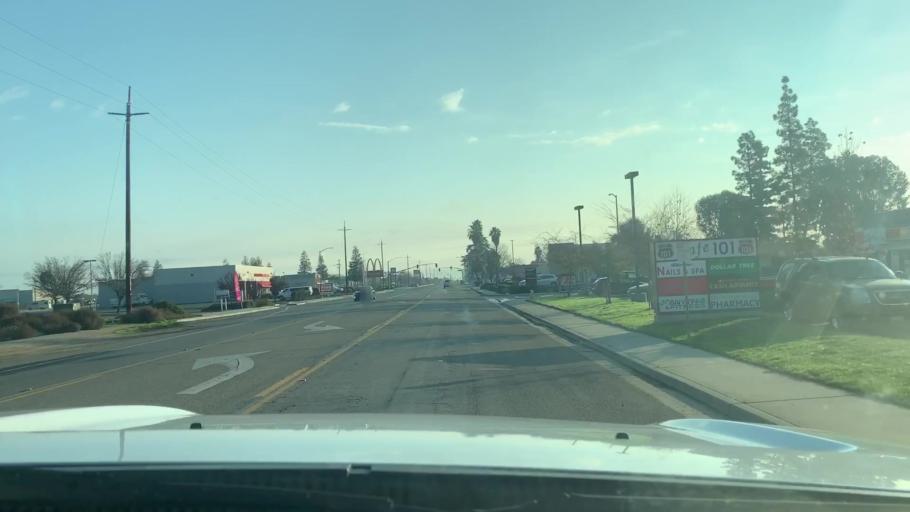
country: US
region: California
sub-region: Kern County
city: Wasco
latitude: 35.6015
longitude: -119.3522
